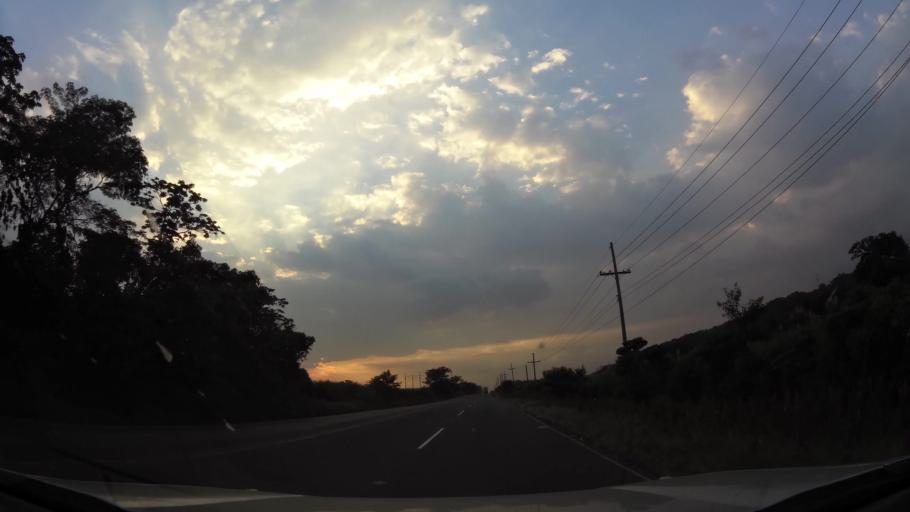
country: GT
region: Escuintla
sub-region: Municipio de Masagua
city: Masagua
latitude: 14.2676
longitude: -90.8766
